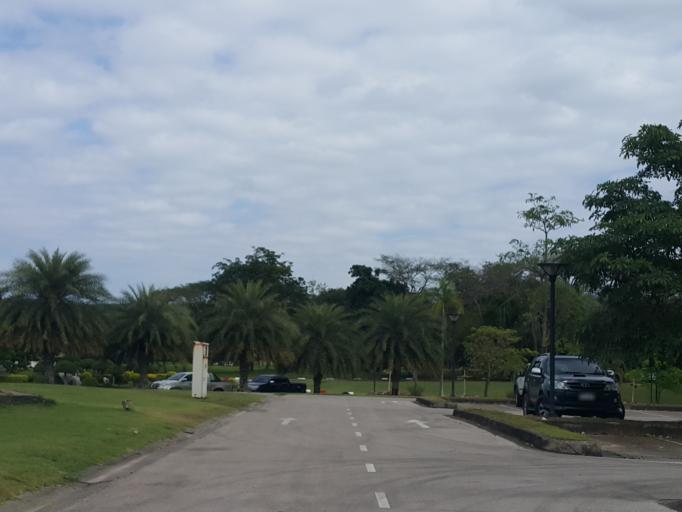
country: TH
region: Lampang
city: Mae Mo
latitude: 18.3200
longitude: 99.7433
